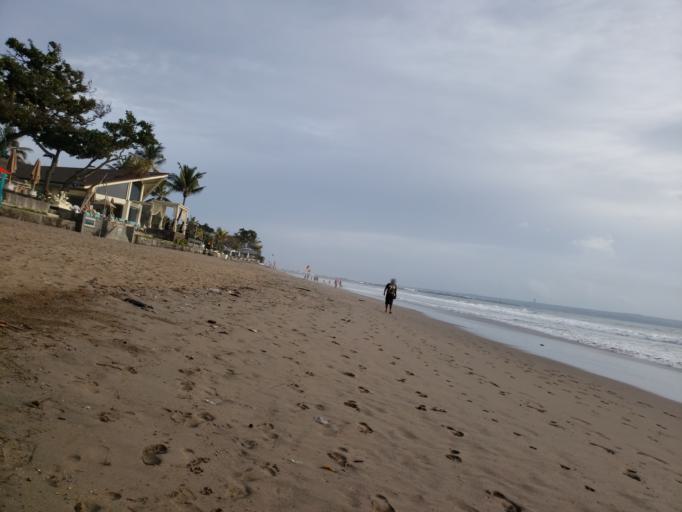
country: ID
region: Bali
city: Kuta
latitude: -8.6855
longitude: 115.1531
